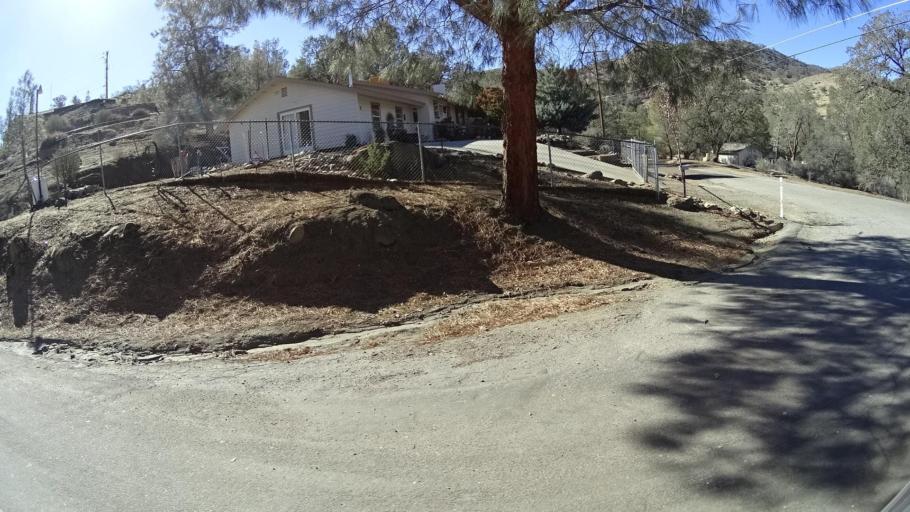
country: US
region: California
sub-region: Kern County
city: Wofford Heights
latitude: 35.7069
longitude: -118.4736
